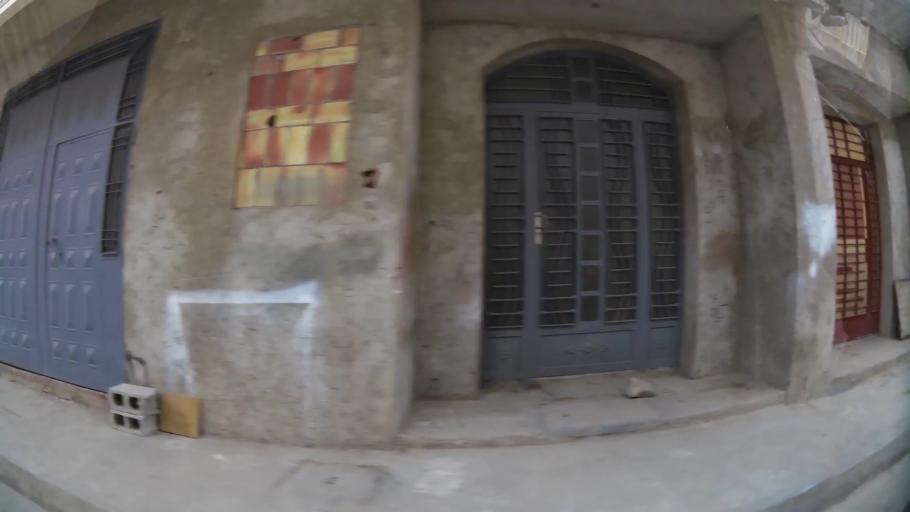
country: MA
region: Oriental
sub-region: Nador
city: Nador
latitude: 35.1599
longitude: -2.9368
